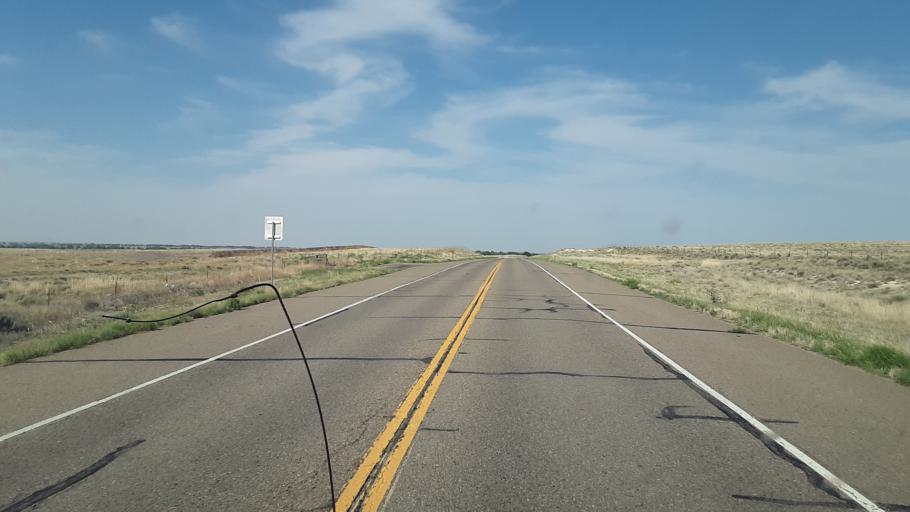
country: US
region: Colorado
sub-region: Bent County
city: Las Animas
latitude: 38.0520
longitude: -103.3530
